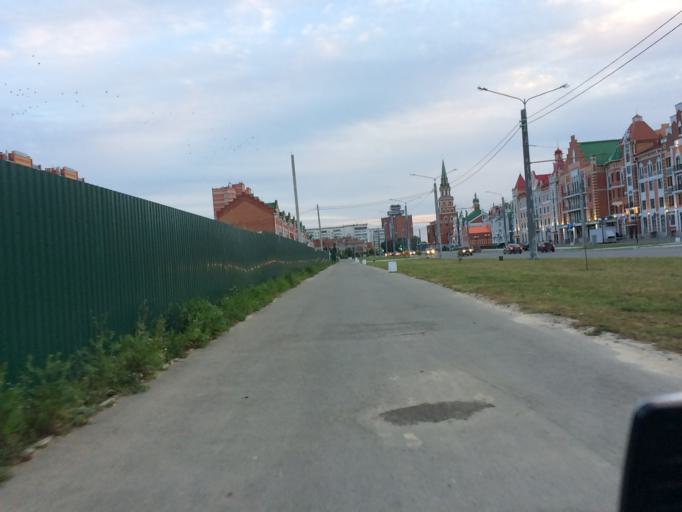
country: RU
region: Mariy-El
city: Yoshkar-Ola
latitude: 56.6352
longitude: 47.9119
